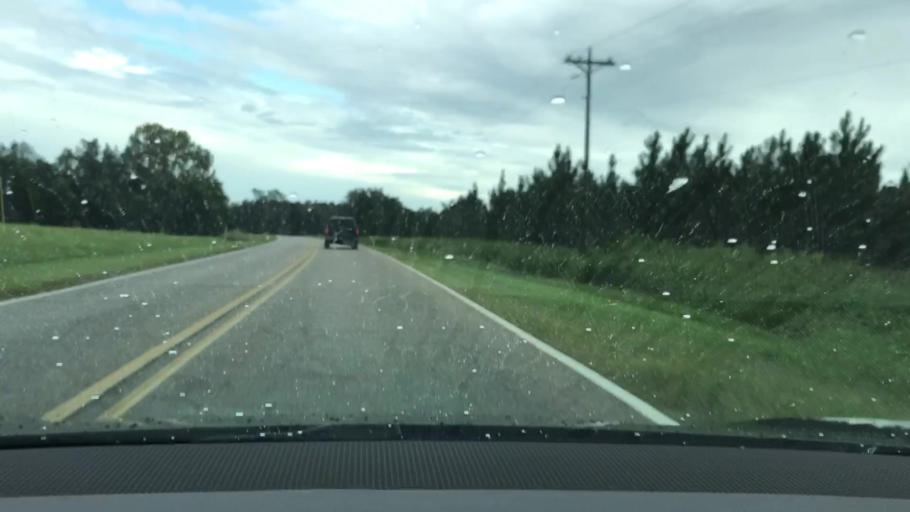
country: US
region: Alabama
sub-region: Geneva County
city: Samson
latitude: 31.1309
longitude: -86.1328
